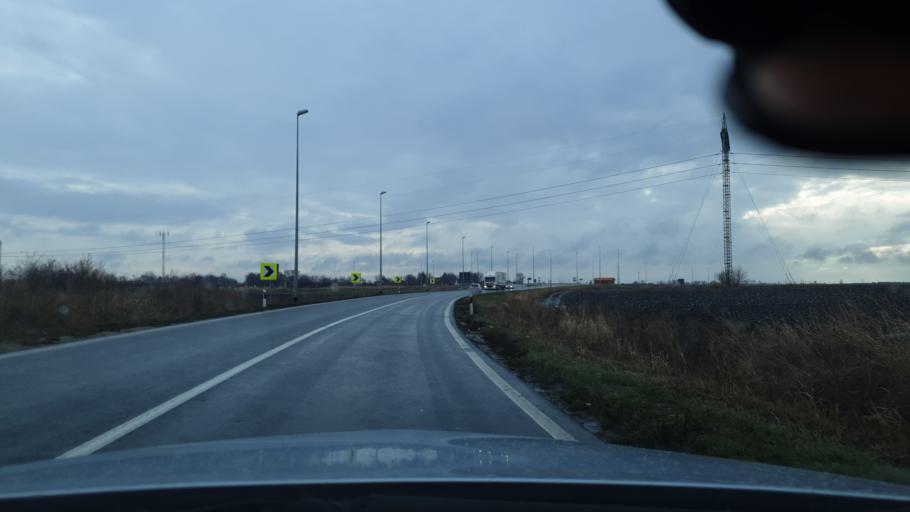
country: RS
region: Autonomna Pokrajina Vojvodina
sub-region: Juznobanatski Okrug
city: Kovin
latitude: 44.8255
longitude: 20.8495
